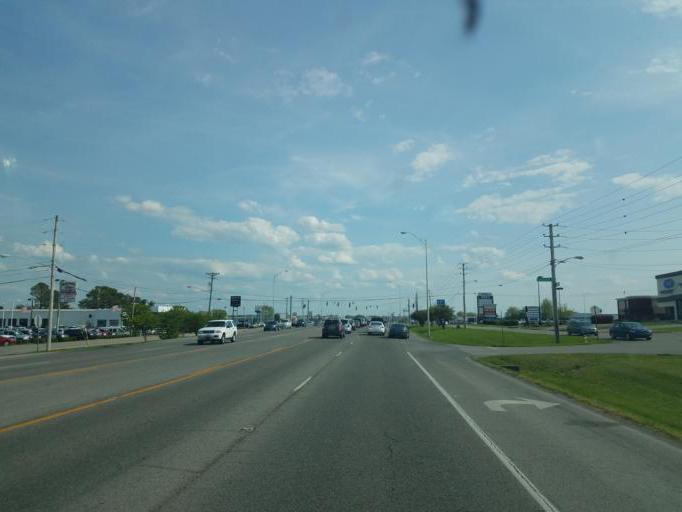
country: US
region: Kentucky
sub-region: Warren County
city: Bowling Green
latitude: 36.9609
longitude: -86.4301
